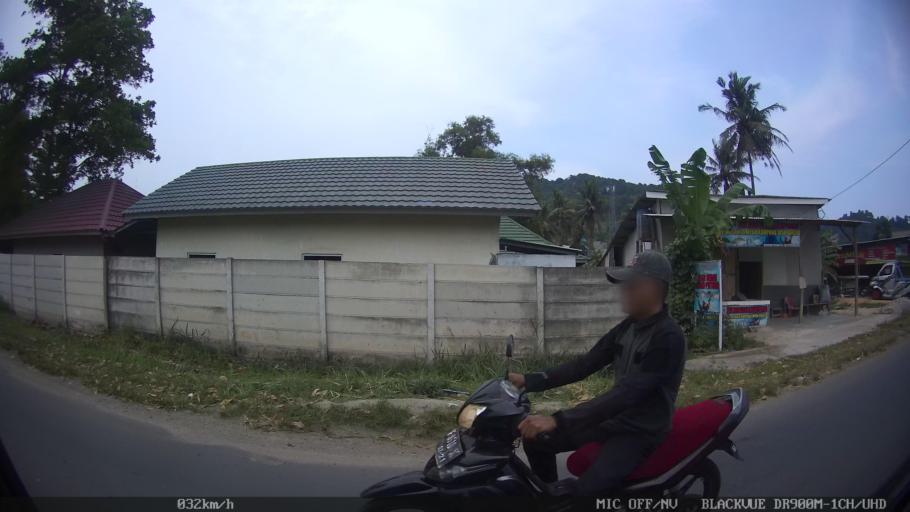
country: ID
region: Lampung
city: Panjang
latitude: -5.4140
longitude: 105.3228
